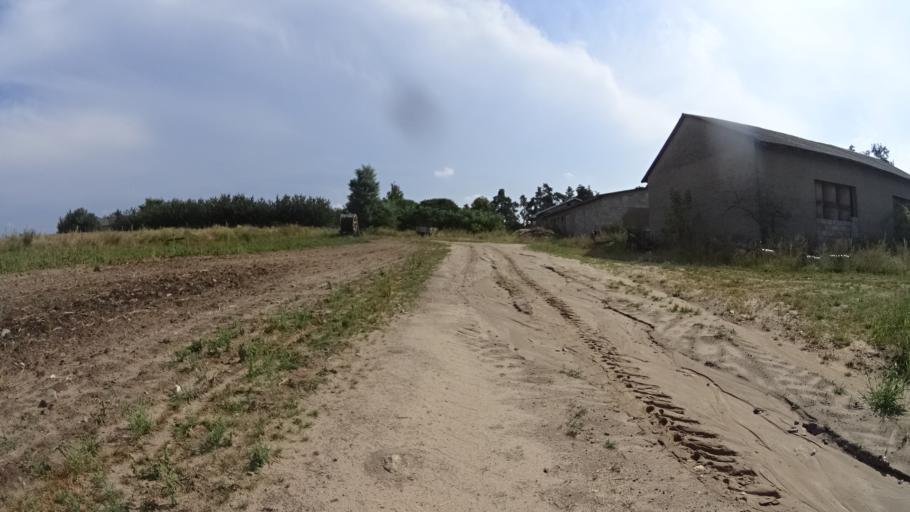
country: PL
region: Masovian Voivodeship
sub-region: Powiat grojecki
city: Goszczyn
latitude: 51.6871
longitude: 20.8407
